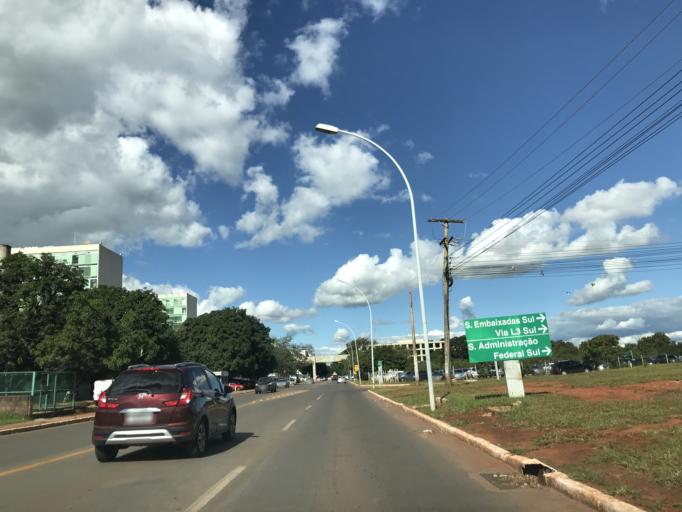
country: BR
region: Federal District
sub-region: Brasilia
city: Brasilia
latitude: -15.7995
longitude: -47.8743
